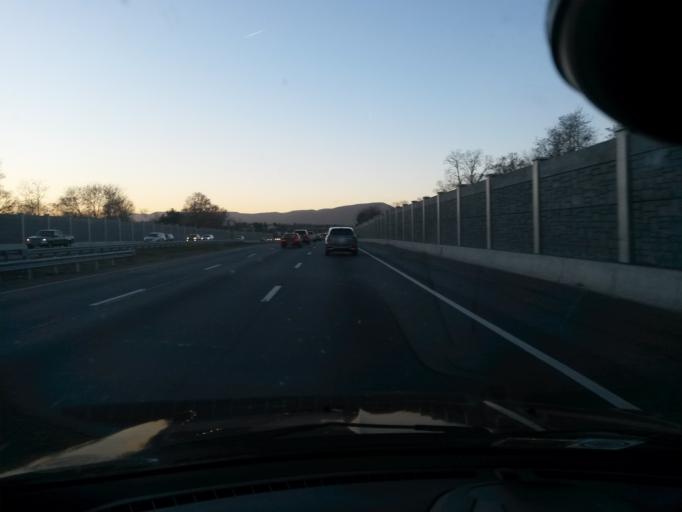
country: US
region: Virginia
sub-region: City of Roanoke
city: Roanoke
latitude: 37.2939
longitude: -79.9492
